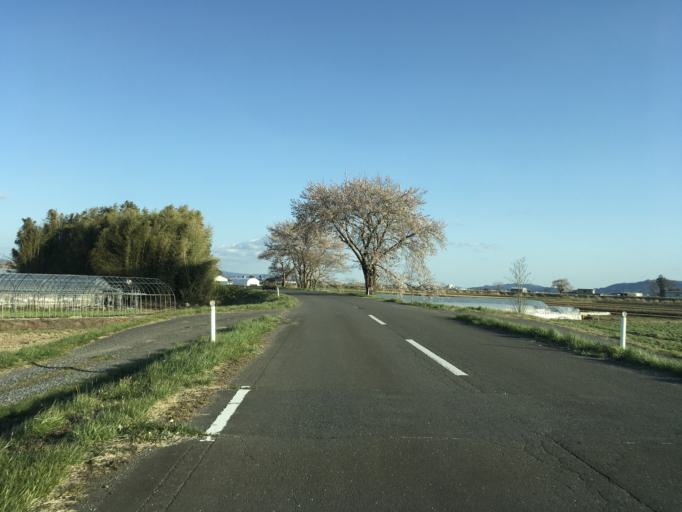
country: JP
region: Miyagi
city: Wakuya
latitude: 38.6450
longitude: 141.1790
